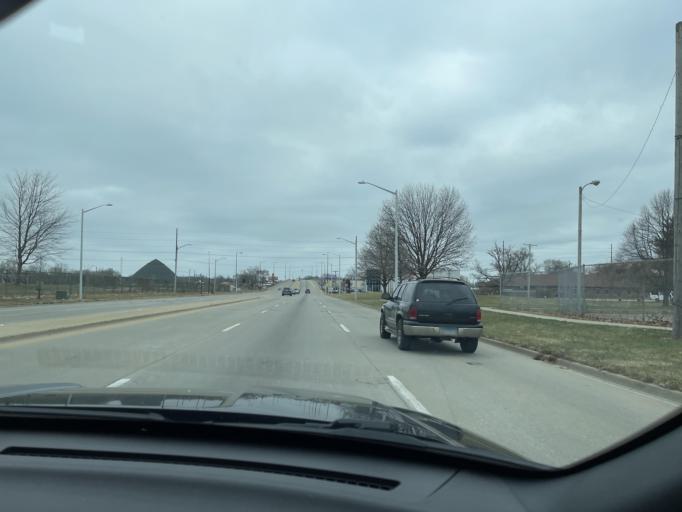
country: US
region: Illinois
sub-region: Sangamon County
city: Springfield
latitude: 39.8033
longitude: -89.6354
